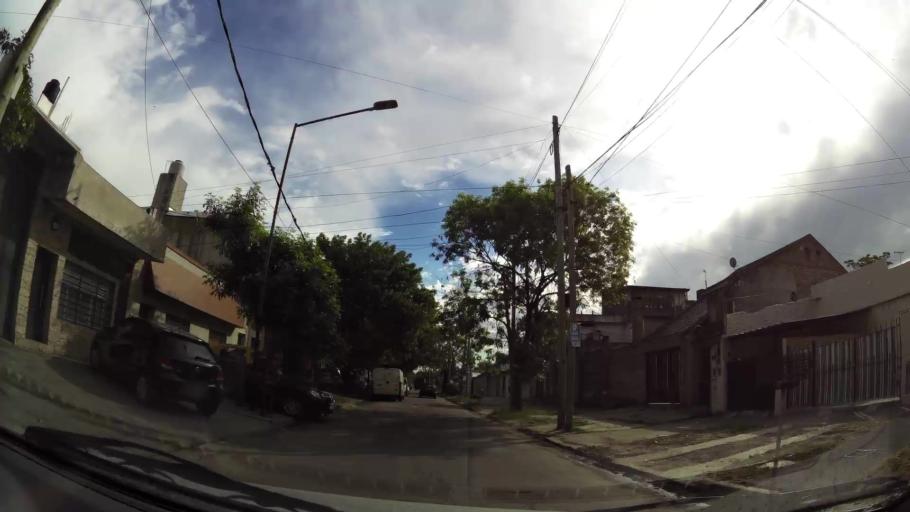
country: AR
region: Buenos Aires
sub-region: Partido de Lanus
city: Lanus
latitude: -34.6912
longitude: -58.3806
